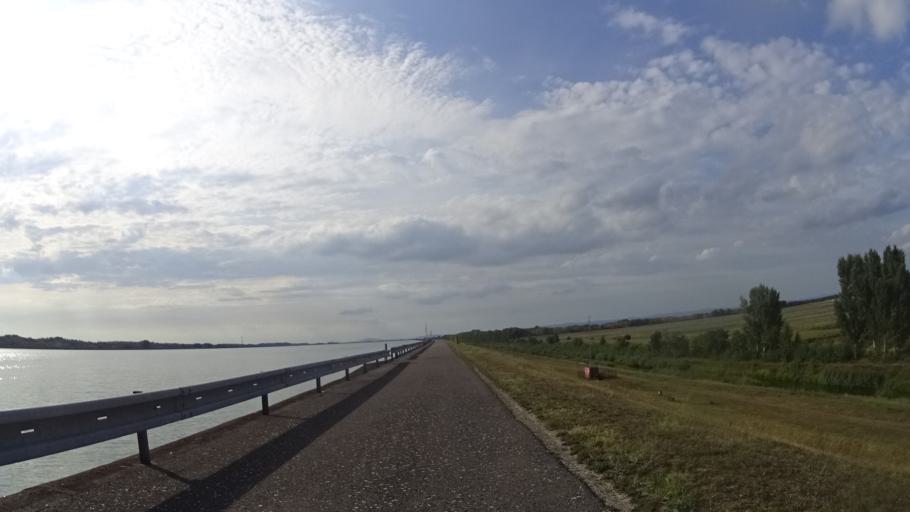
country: HU
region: Gyor-Moson-Sopron
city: Halaszi
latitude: 47.9543
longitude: 17.4333
